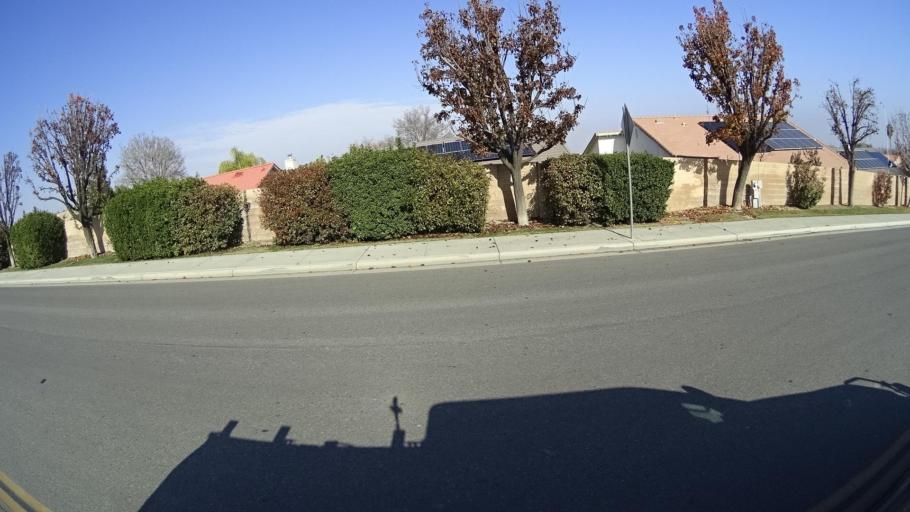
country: US
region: California
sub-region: Kern County
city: Taft Heights
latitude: 35.1366
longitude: -119.4781
